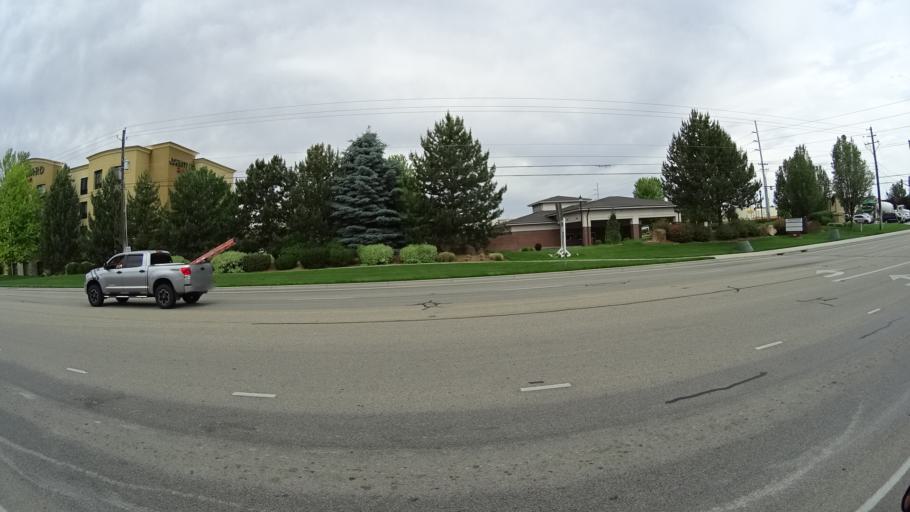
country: US
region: Idaho
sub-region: Ada County
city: Meridian
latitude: 43.5896
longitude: -116.3544
